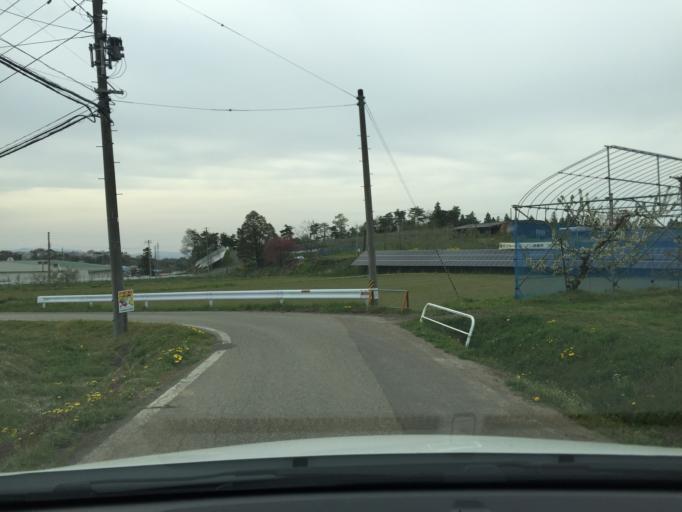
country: JP
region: Fukushima
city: Kitakata
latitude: 37.5543
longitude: 139.9579
